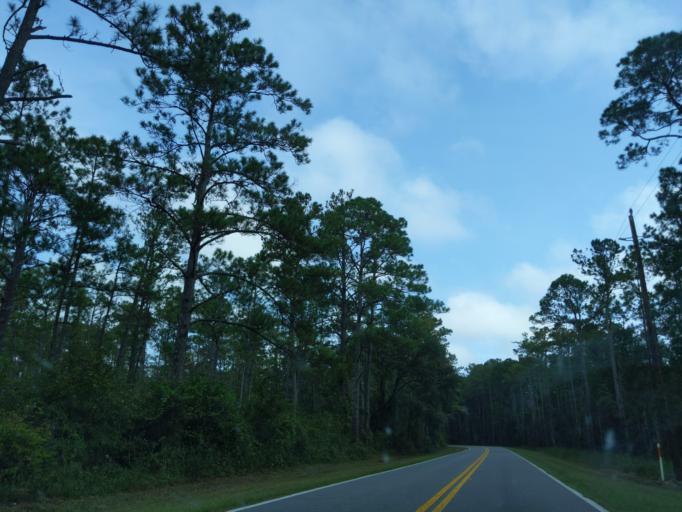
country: US
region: Florida
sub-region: Wakulla County
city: Crawfordville
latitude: 30.1060
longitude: -84.3081
